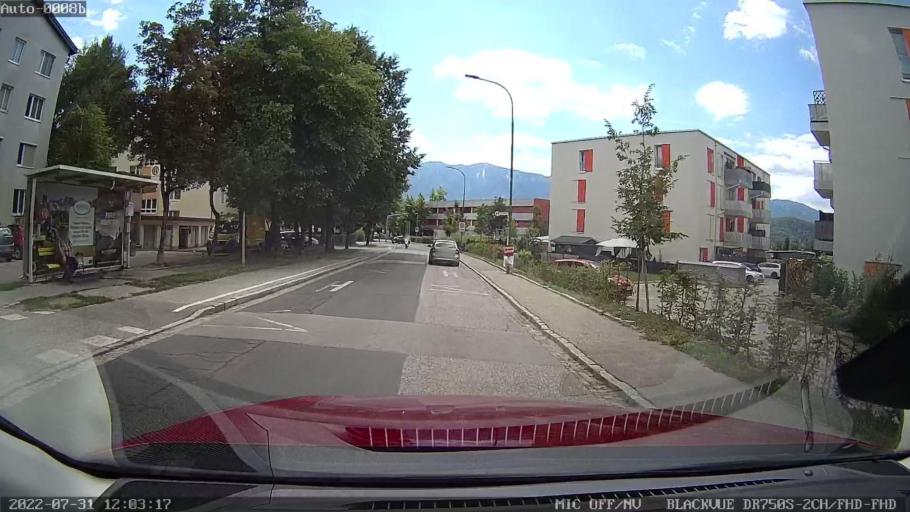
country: AT
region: Carinthia
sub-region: Villach Stadt
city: Villach
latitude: 46.6027
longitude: 13.8459
